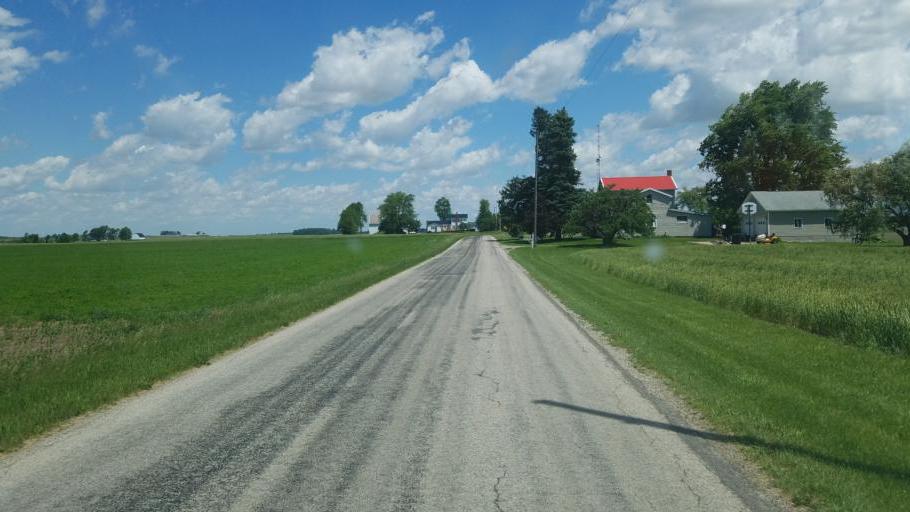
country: US
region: Ohio
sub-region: Richland County
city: Shelby
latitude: 40.8988
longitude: -82.7052
